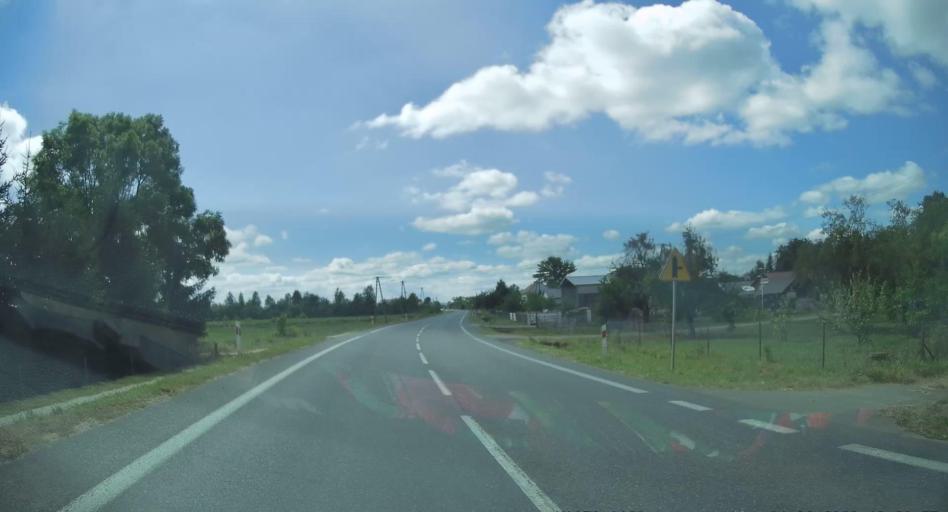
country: PL
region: Subcarpathian Voivodeship
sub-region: Powiat mielecki
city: Przeclaw
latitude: 50.1616
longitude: 21.4868
